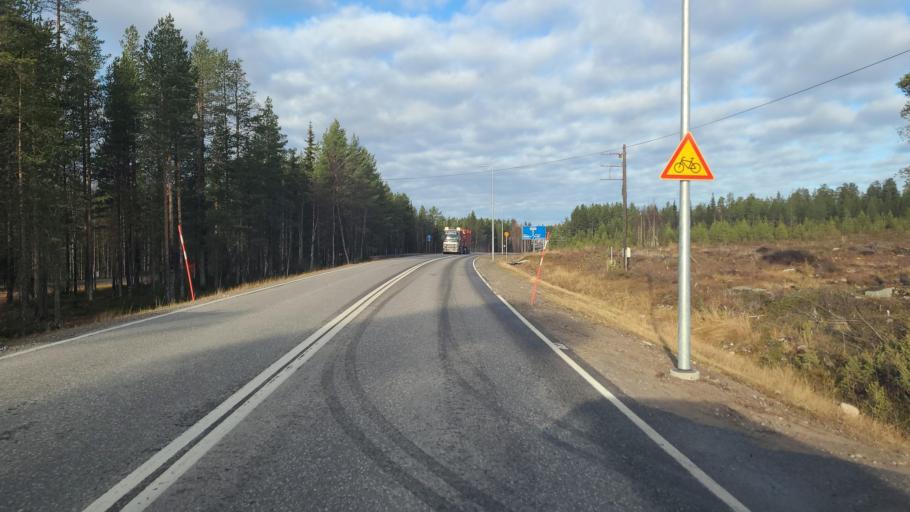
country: FI
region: Lapland
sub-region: Itae-Lappi
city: Posio
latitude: 66.1053
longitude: 28.1828
